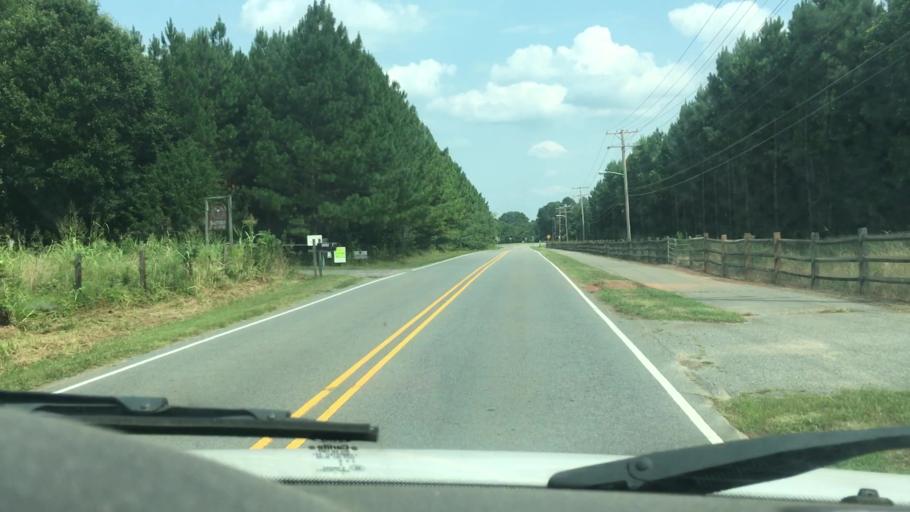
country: US
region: North Carolina
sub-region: Gaston County
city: Davidson
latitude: 35.4860
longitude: -80.8230
